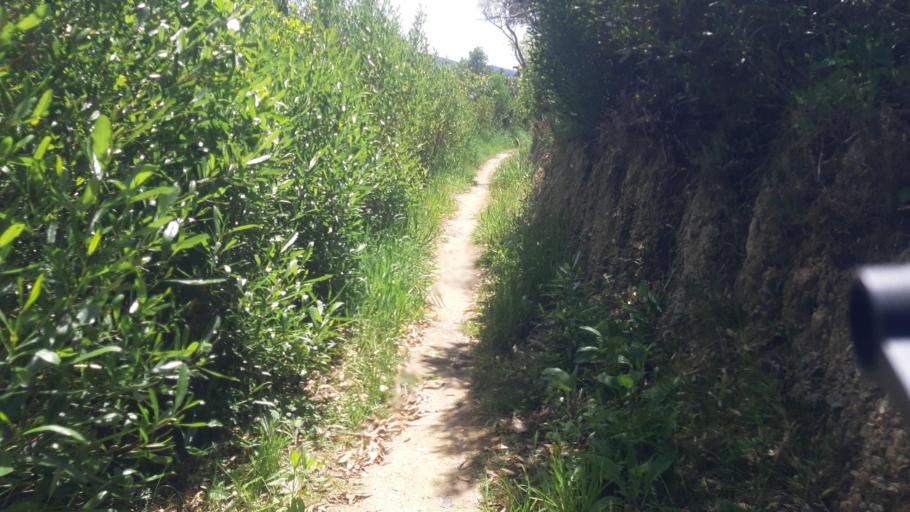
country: NZ
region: Marlborough
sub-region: Marlborough District
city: Picton
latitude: -41.2645
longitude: 174.0299
